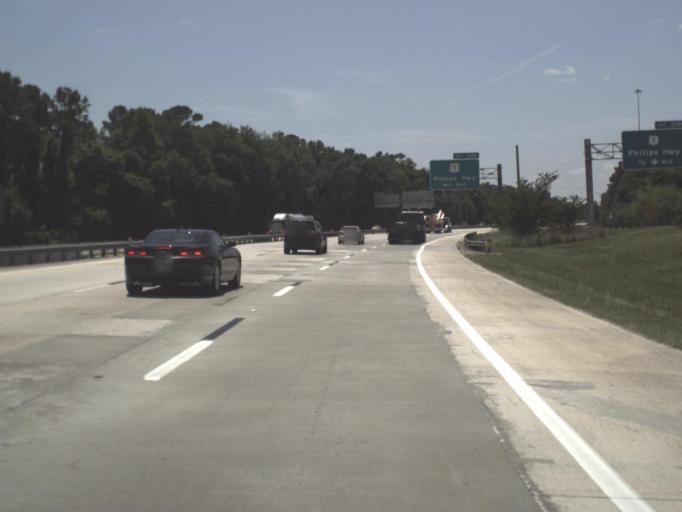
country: US
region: Florida
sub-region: Saint Johns County
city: Fruit Cove
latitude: 30.1970
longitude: -81.5565
